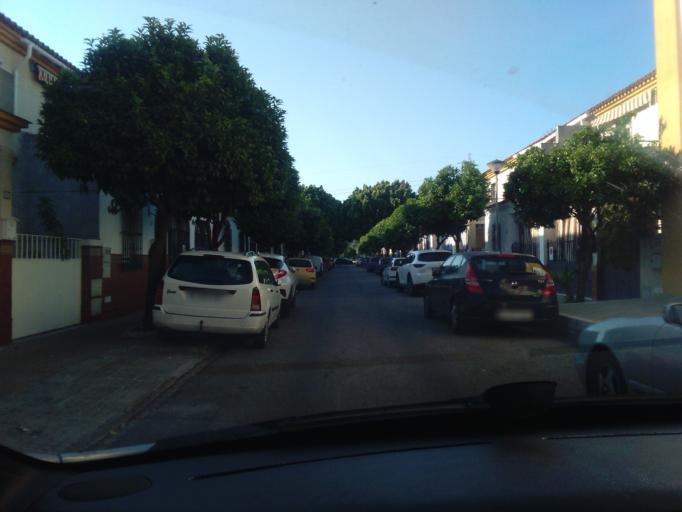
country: ES
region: Andalusia
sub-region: Provincia de Sevilla
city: Sevilla
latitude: 37.3888
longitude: -5.9176
